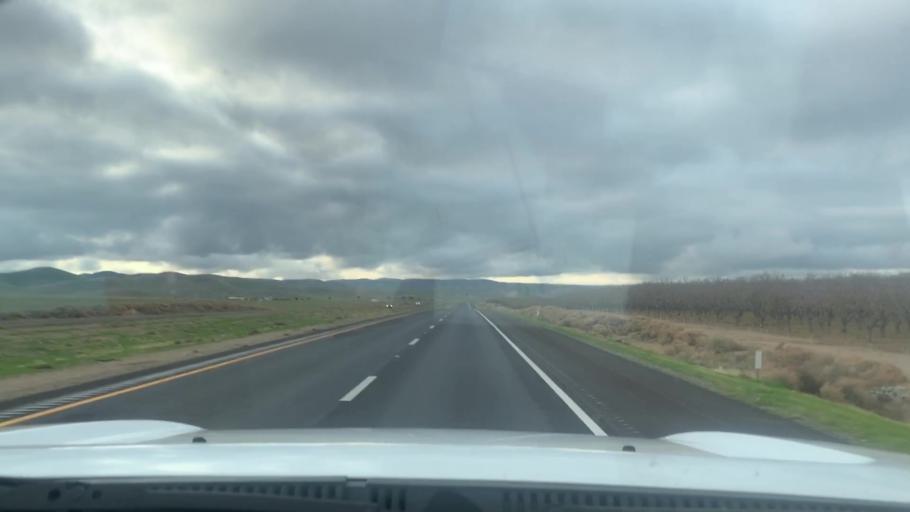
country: US
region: California
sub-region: Kern County
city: Lost Hills
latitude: 35.6145
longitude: -119.9502
